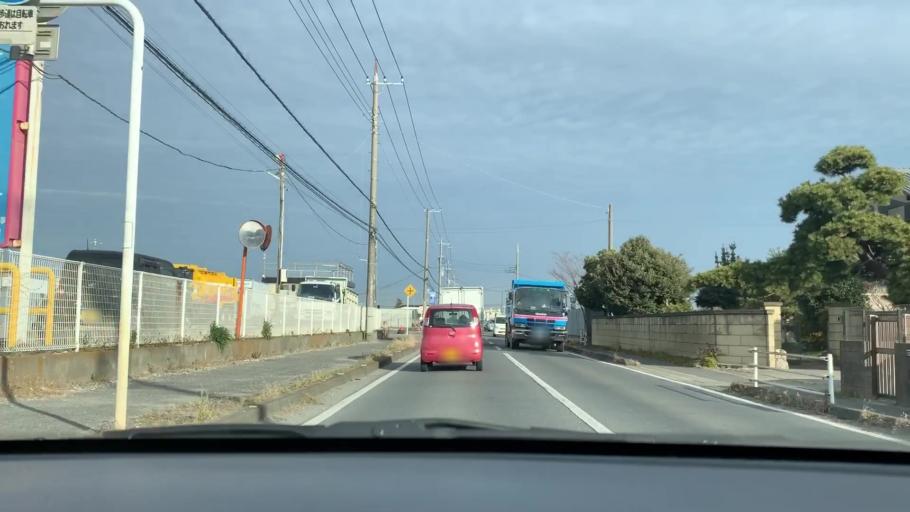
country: JP
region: Chiba
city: Matsudo
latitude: 35.8179
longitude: 139.8954
